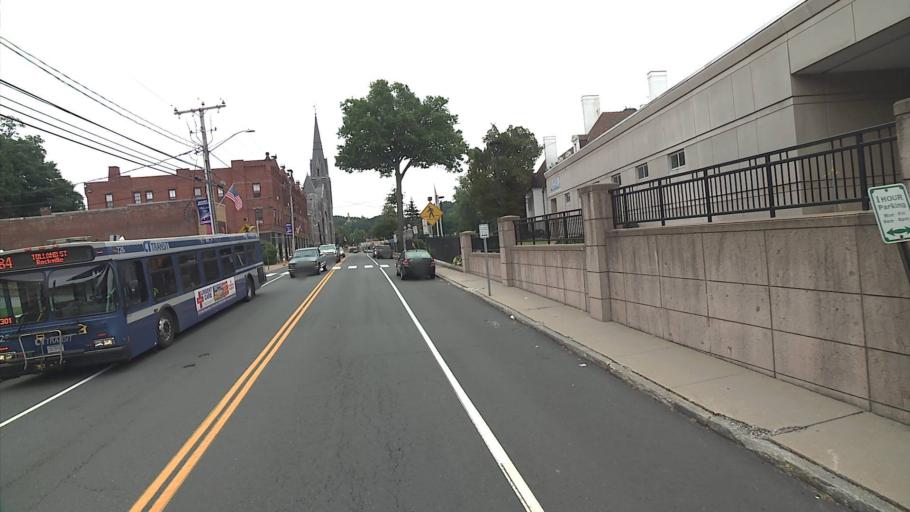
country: US
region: Connecticut
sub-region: Tolland County
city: Rockville
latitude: 41.8669
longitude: -72.4514
